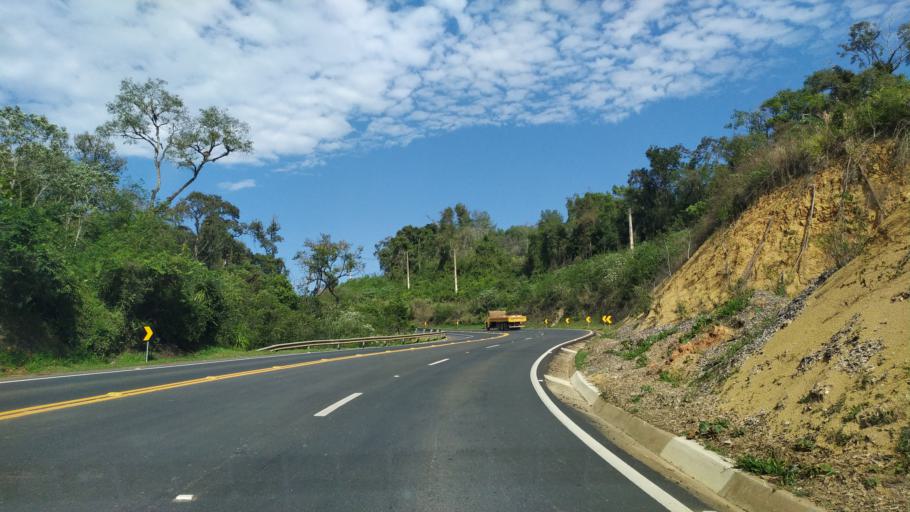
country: BR
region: Parana
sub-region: Telemaco Borba
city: Telemaco Borba
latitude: -24.2942
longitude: -50.7025
